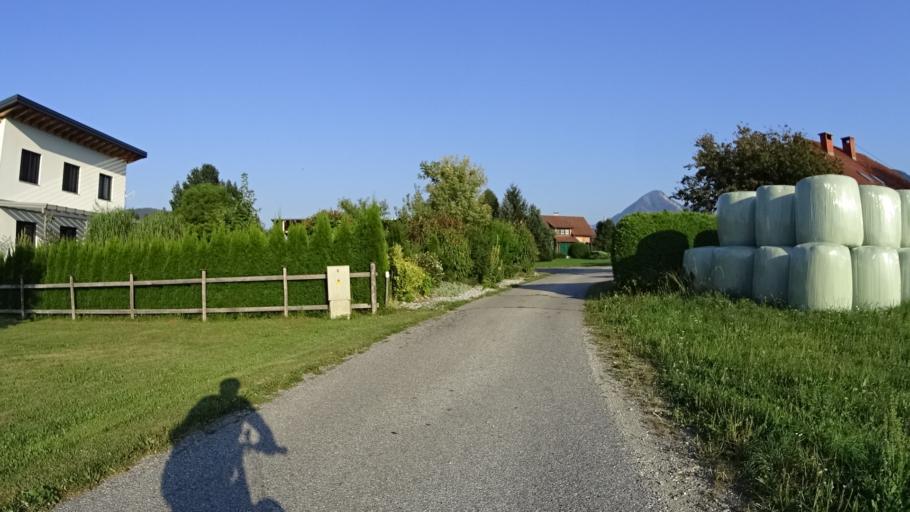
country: AT
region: Carinthia
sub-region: Politischer Bezirk Villach Land
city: Sankt Jakob
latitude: 46.5532
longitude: 14.0635
